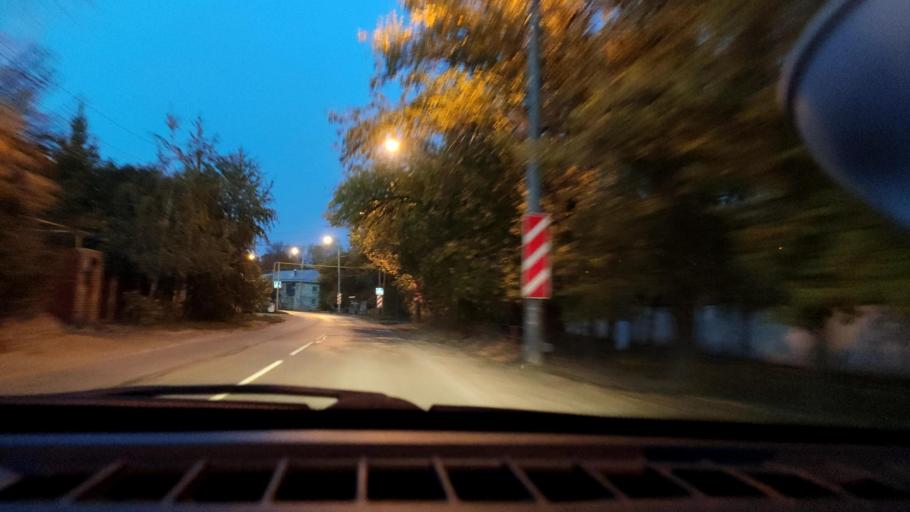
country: RU
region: Samara
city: Samara
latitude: 53.1369
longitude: 50.1233
